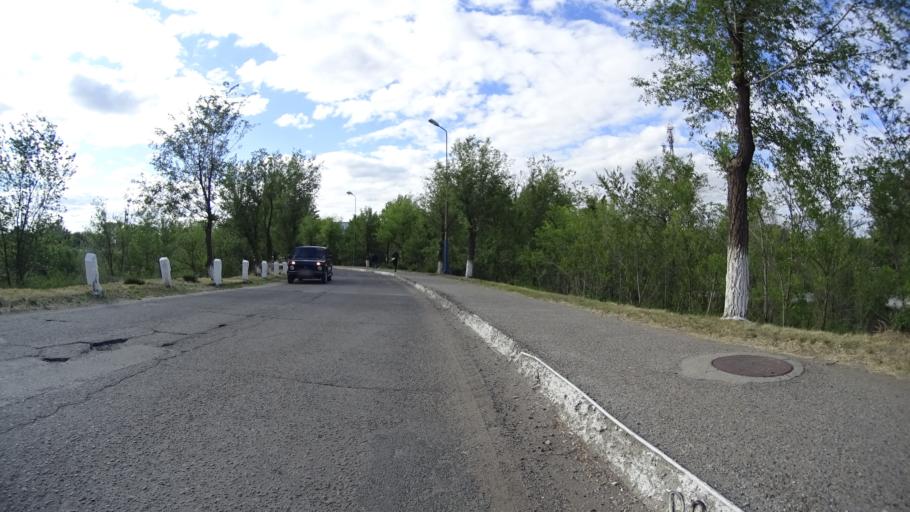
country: RU
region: Chelyabinsk
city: Troitsk
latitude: 54.0402
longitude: 61.6396
